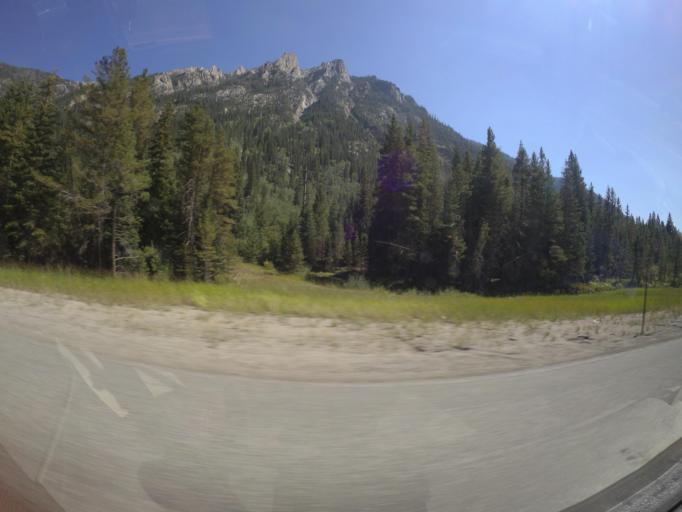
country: US
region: Colorado
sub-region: Summit County
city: Frisco
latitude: 39.5520
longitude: -106.1374
